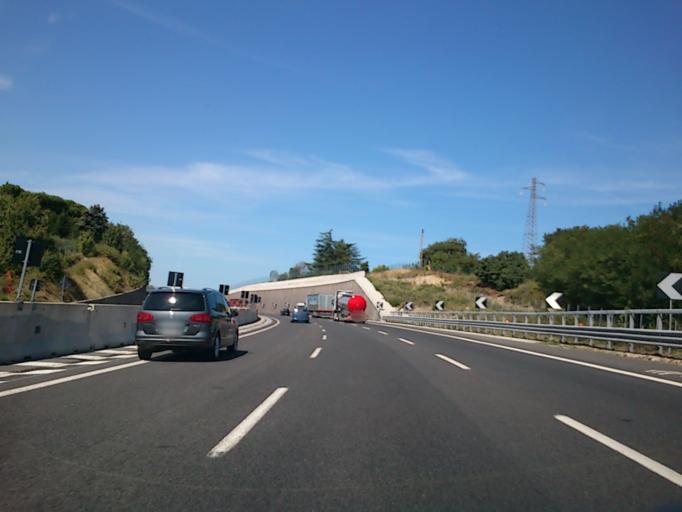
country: IT
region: The Marches
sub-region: Provincia di Pesaro e Urbino
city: Fenile
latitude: 43.8566
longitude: 12.9441
